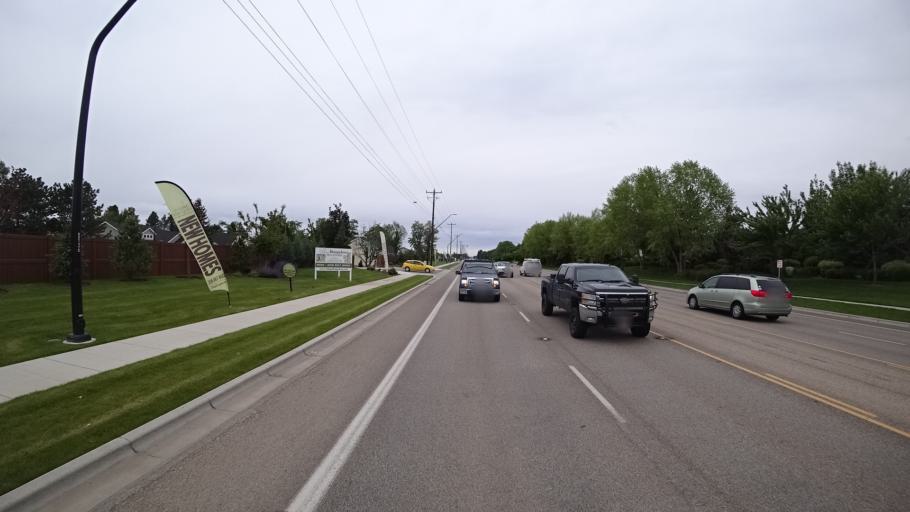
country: US
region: Idaho
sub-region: Ada County
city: Meridian
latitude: 43.6337
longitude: -116.3622
